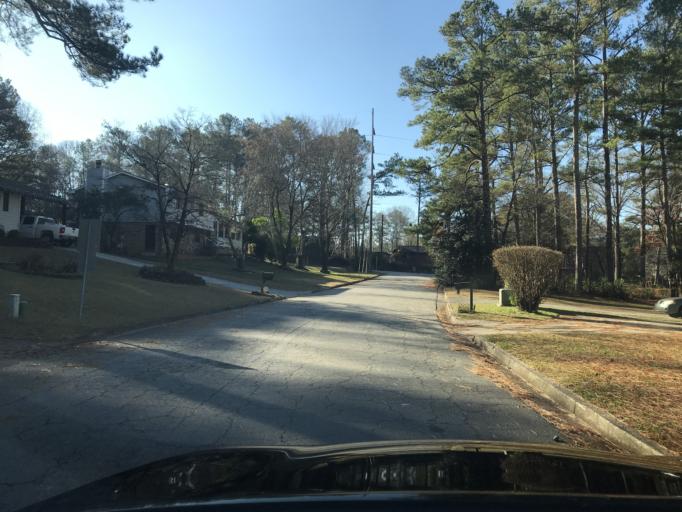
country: US
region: Georgia
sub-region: Clayton County
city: Riverdale
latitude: 33.5571
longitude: -84.3755
